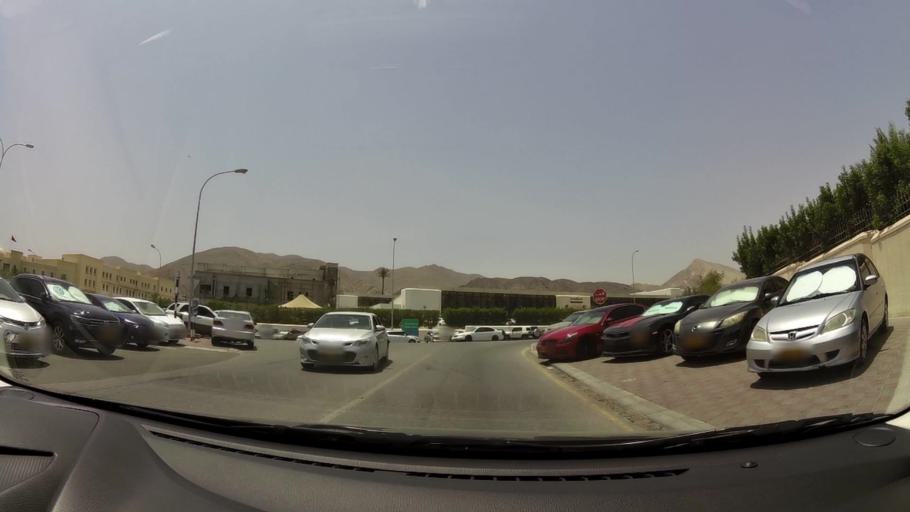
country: OM
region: Muhafazat Masqat
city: Bawshar
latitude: 23.5806
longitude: 58.4310
